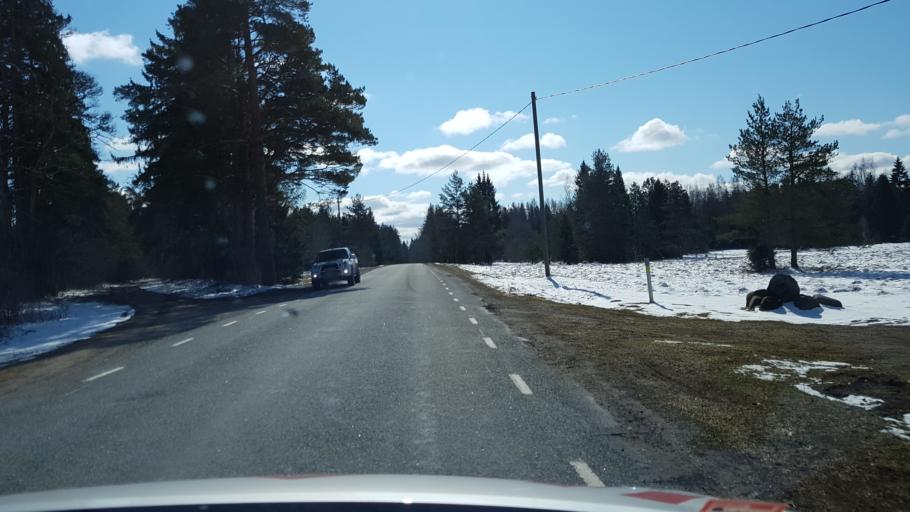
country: EE
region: Laeaene-Virumaa
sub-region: Tapa vald
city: Tapa
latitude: 59.5034
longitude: 25.9658
